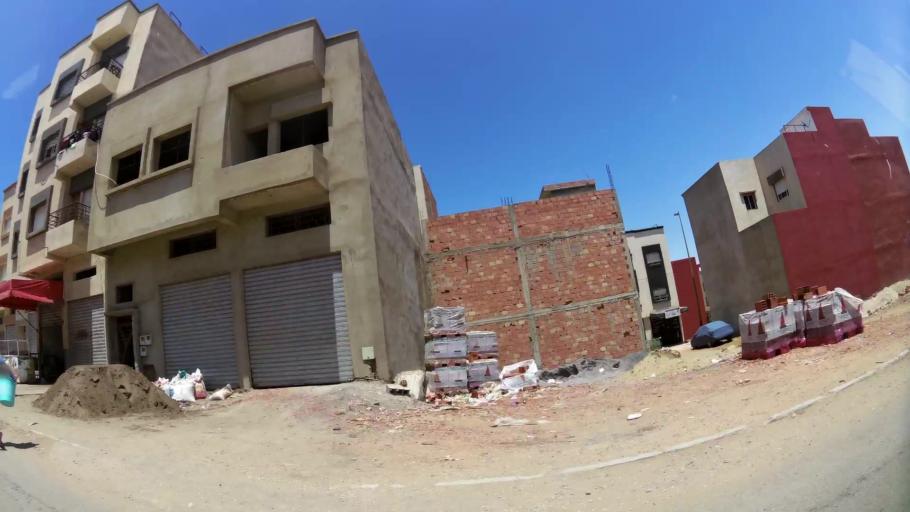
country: MA
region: Gharb-Chrarda-Beni Hssen
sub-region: Kenitra Province
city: Kenitra
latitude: 34.2330
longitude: -6.6155
